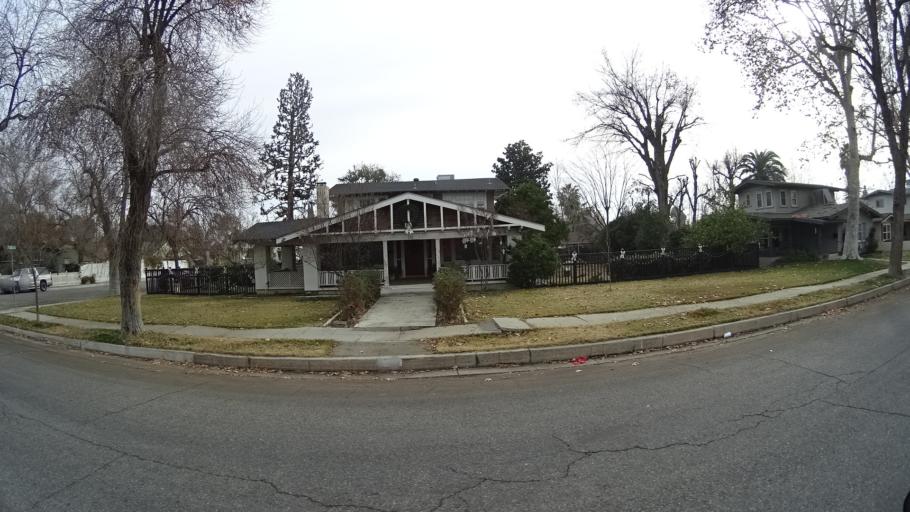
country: US
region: California
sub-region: Kern County
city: Bakersfield
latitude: 35.3567
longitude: -119.0255
